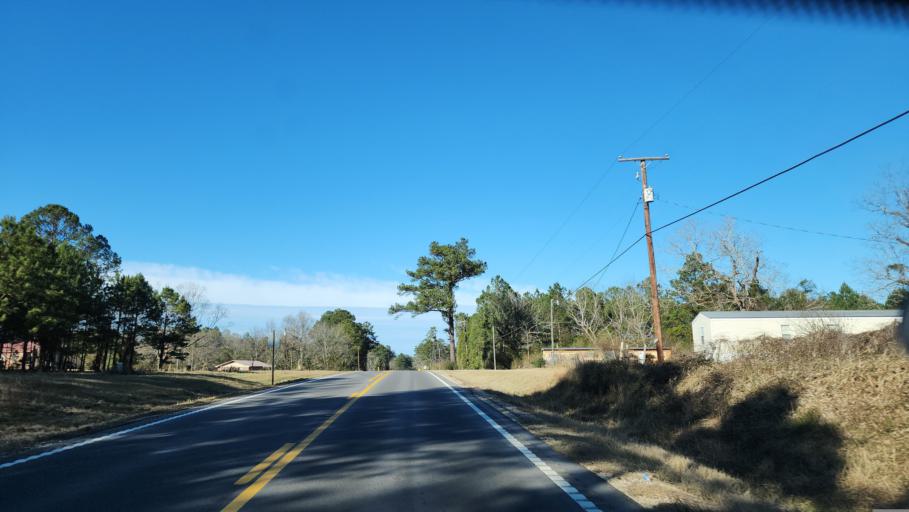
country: US
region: Mississippi
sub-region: Wayne County
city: Waynesboro
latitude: 31.7109
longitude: -88.6445
